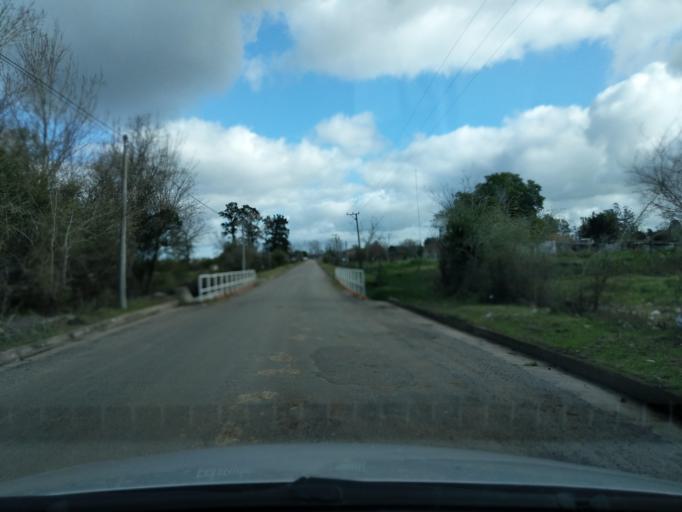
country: UY
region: Florida
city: Florida
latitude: -34.1077
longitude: -56.2188
